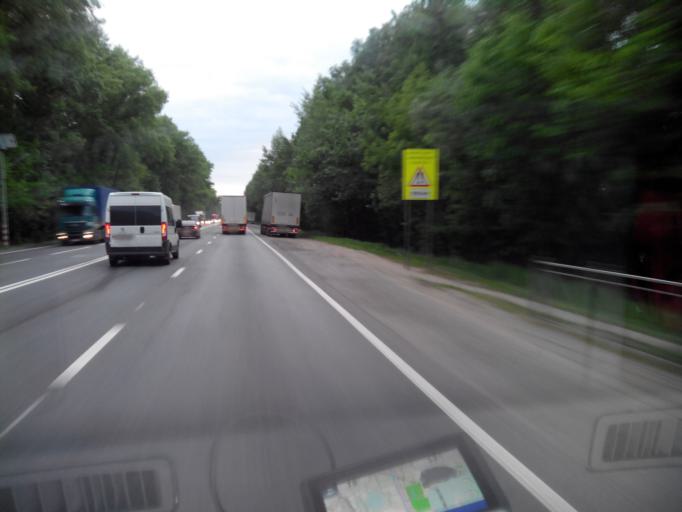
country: RU
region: Penza
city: Zarechnyy
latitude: 53.2216
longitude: 45.2099
